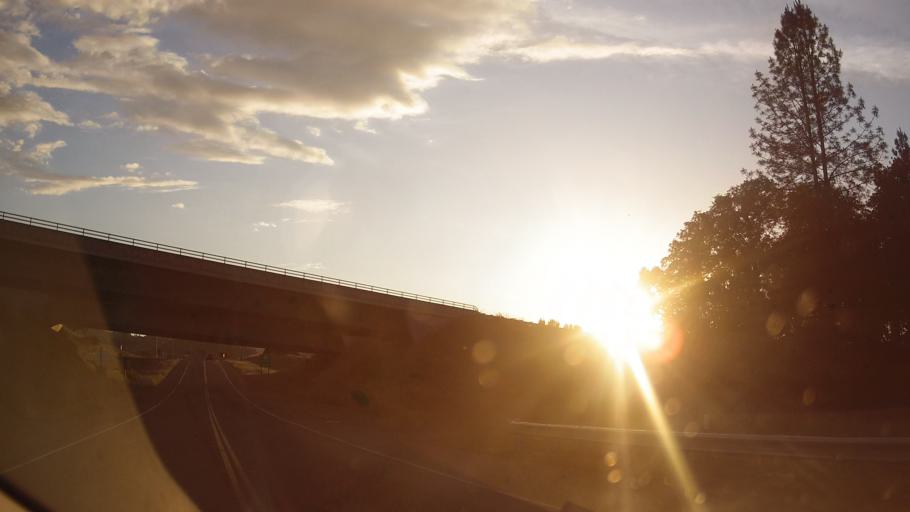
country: US
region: California
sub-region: Mendocino County
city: Willits
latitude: 39.3755
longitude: -123.3258
